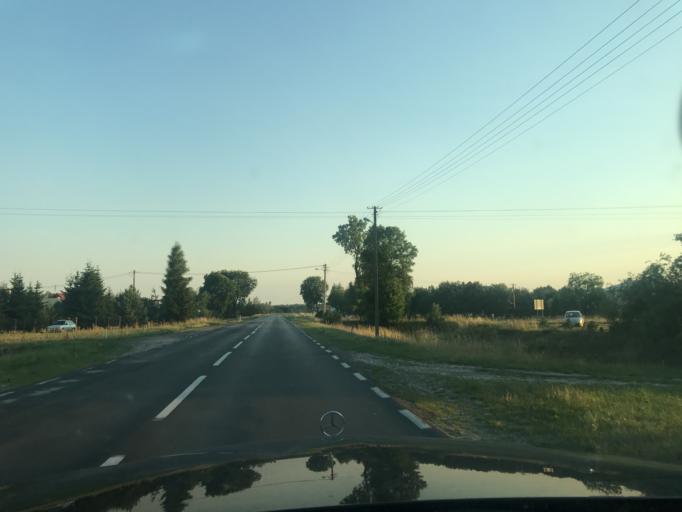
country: PL
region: Lublin Voivodeship
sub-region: Powiat lubartowski
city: Lubartow
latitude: 51.4850
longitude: 22.6264
